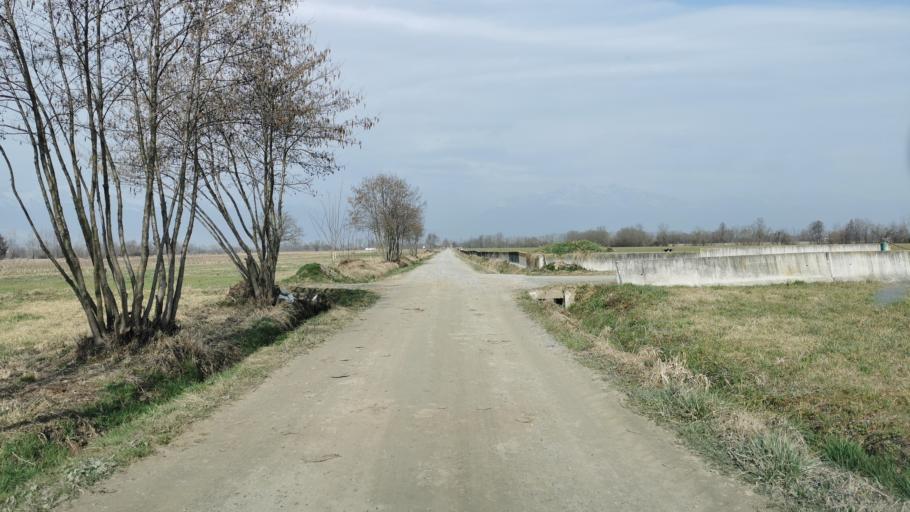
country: IT
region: Piedmont
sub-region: Provincia di Torino
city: Rivarossa
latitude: 45.2733
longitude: 7.7028
